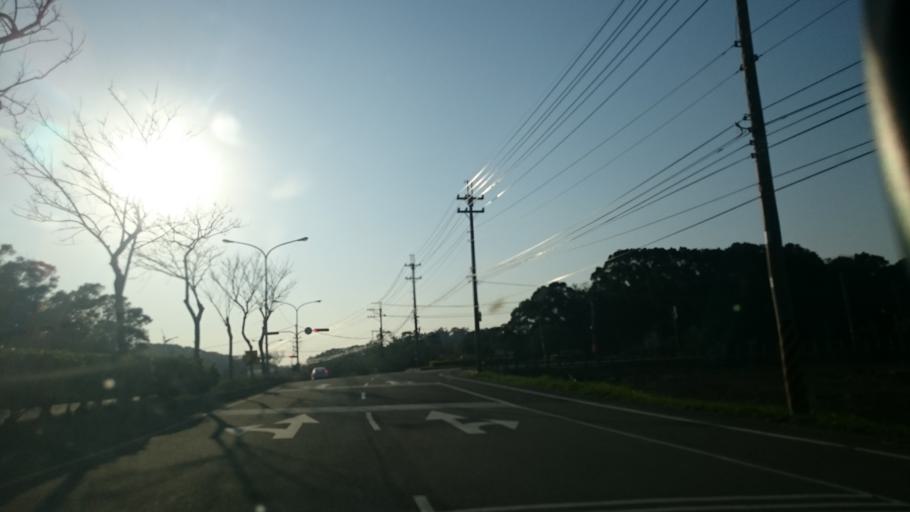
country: TW
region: Taiwan
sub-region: Miaoli
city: Miaoli
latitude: 24.6311
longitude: 120.8250
